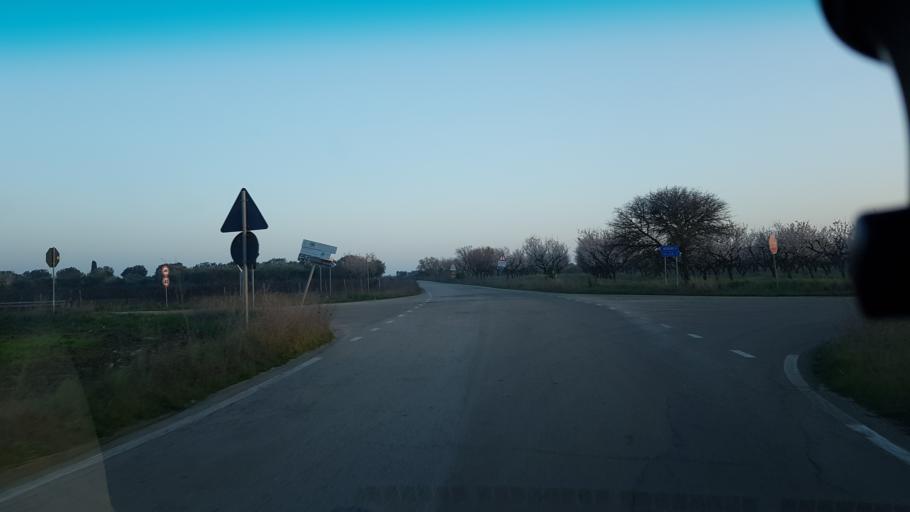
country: IT
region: Apulia
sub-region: Provincia di Brindisi
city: Mesagne
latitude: 40.6202
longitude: 17.7844
